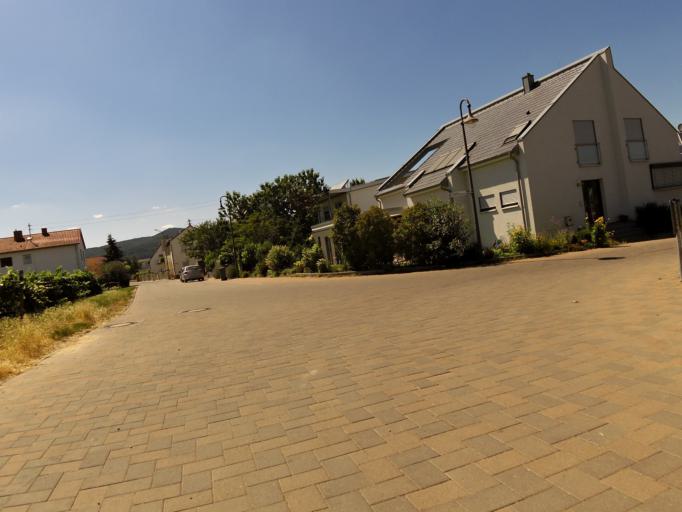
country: DE
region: Rheinland-Pfalz
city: Ruppertsberg
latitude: 49.3973
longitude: 8.2007
